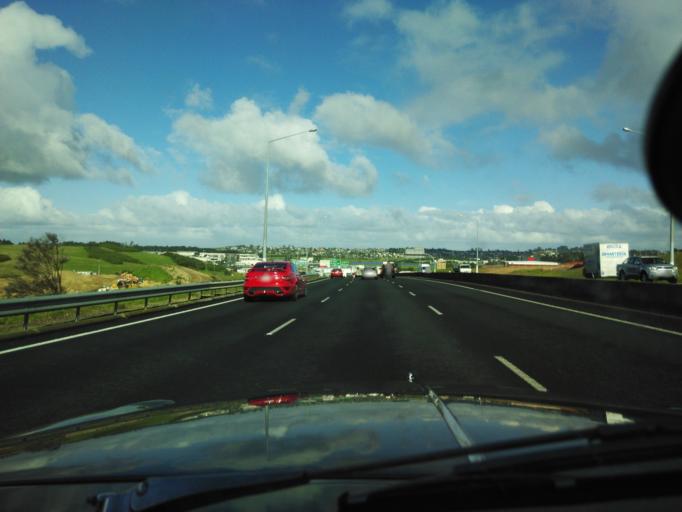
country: NZ
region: Auckland
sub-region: Auckland
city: Rothesay Bay
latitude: -36.7293
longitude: 174.7152
